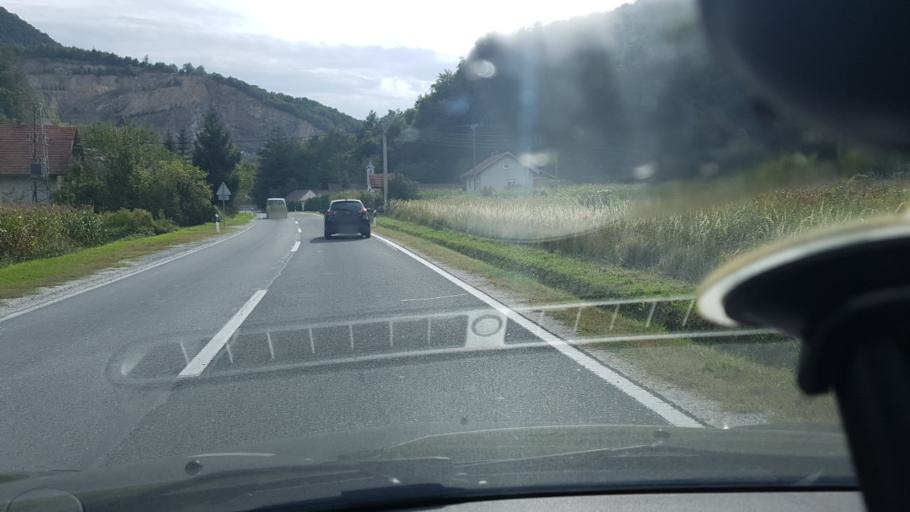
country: HR
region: Varazdinska
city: Lepoglava
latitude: 46.1964
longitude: 15.9950
